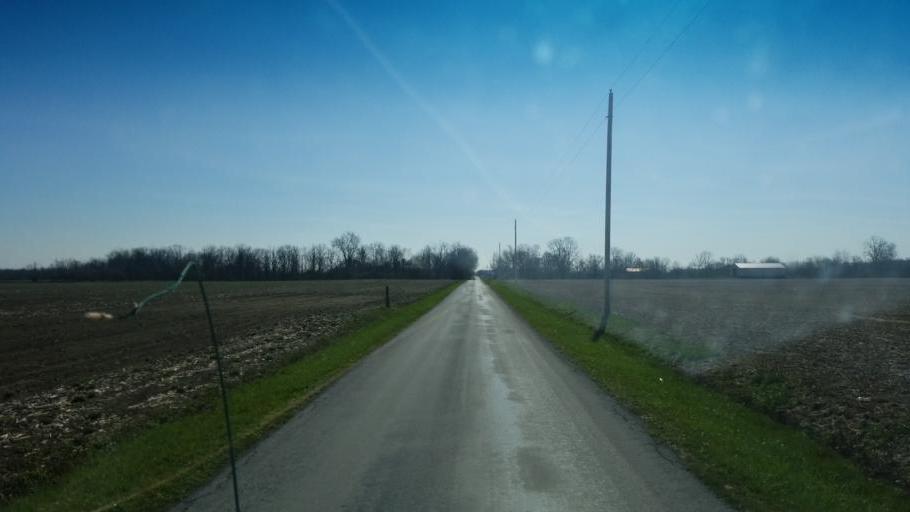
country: US
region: Ohio
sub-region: Hardin County
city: Forest
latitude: 40.7088
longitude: -83.4905
